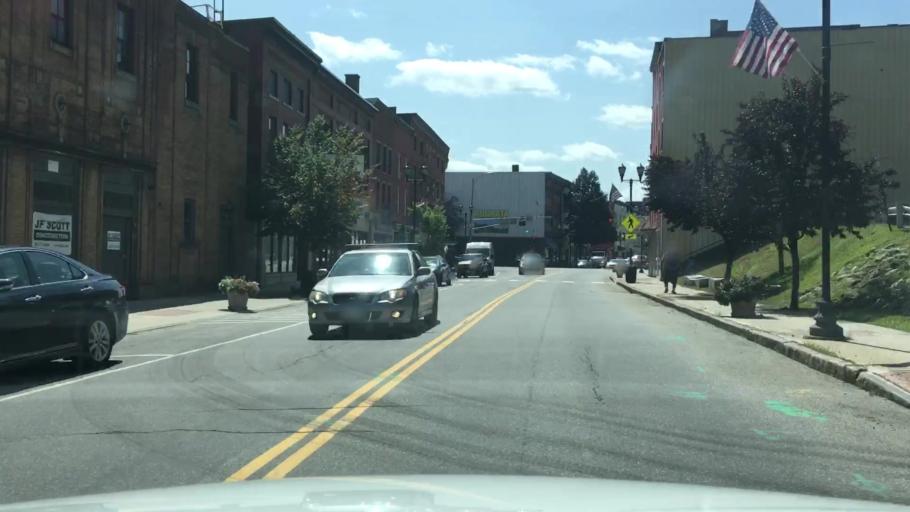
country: US
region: Maine
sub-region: Kennebec County
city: Augusta
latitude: 44.3180
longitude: -69.7733
